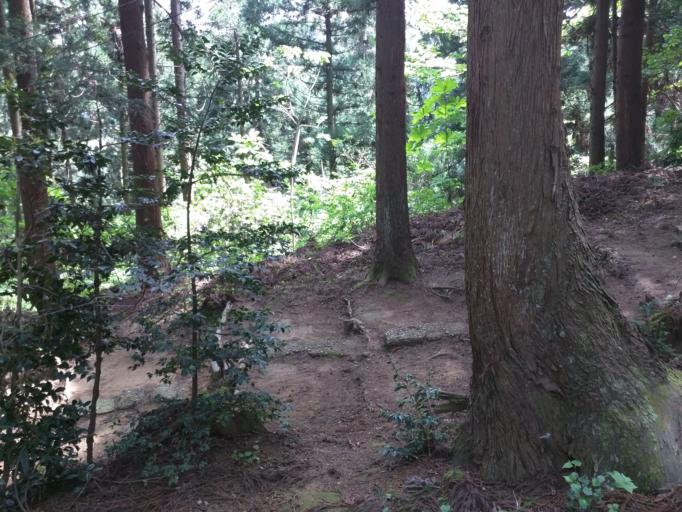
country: JP
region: Niigata
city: Sanjo
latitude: 37.5772
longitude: 138.9570
